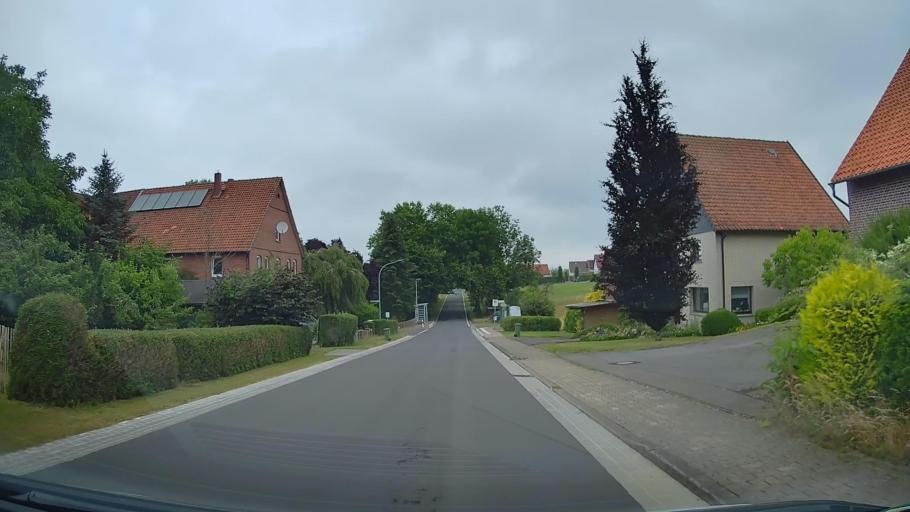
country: DE
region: Lower Saxony
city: Rinteln
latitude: 52.1403
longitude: 9.1003
